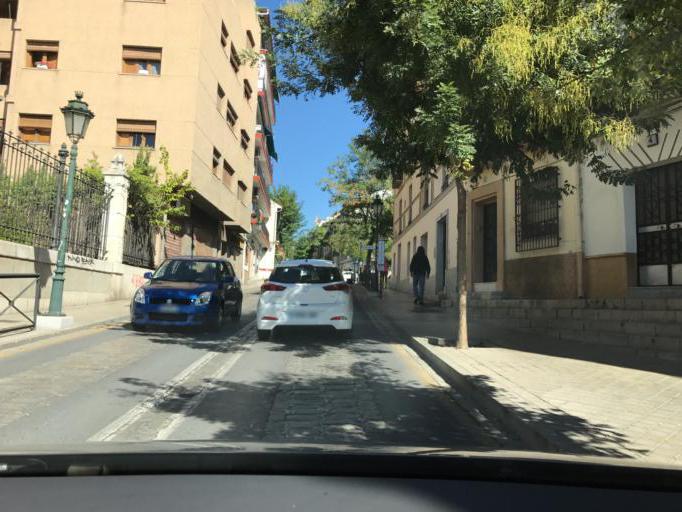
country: ES
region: Andalusia
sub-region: Provincia de Granada
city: Granada
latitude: 37.1850
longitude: -3.6002
